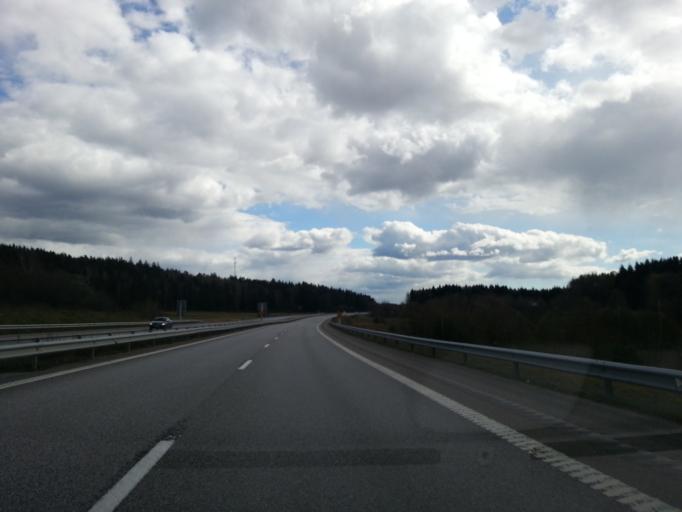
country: SE
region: Vaestra Goetaland
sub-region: Uddevalla Kommun
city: Uddevalla
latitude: 58.3169
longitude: 11.8573
